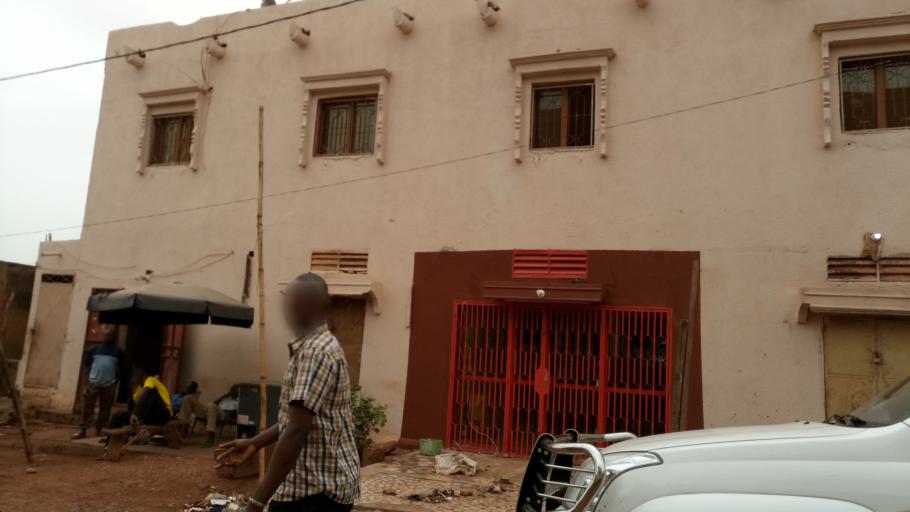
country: ML
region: Bamako
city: Bamako
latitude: 12.5886
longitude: -7.9947
